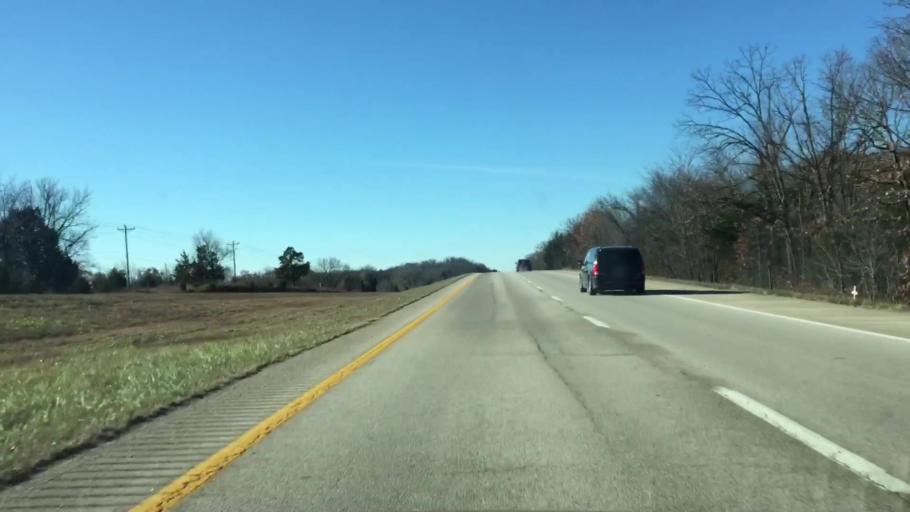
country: US
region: Missouri
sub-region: Cole County
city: Wardsville
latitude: 38.4389
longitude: -92.3056
